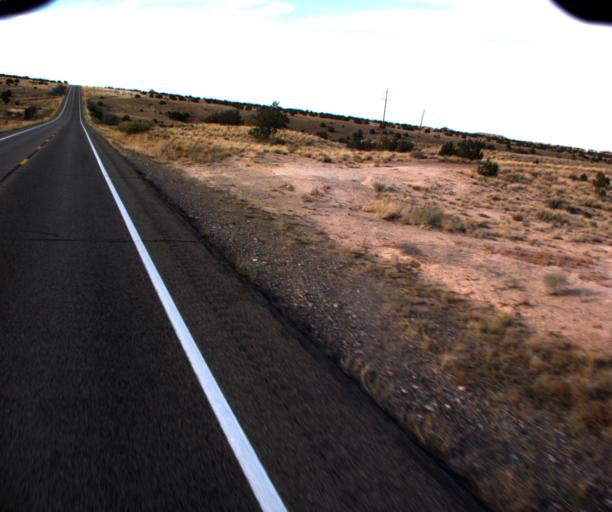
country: US
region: New Mexico
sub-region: San Juan County
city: Shiprock
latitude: 36.8835
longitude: -109.0526
